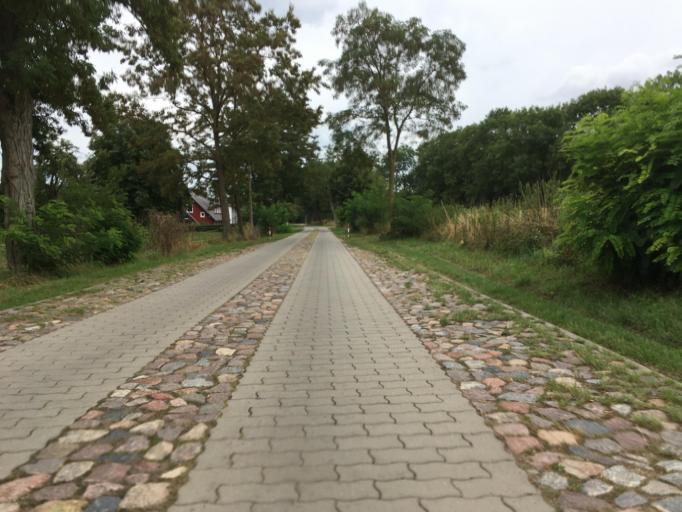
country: DE
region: Brandenburg
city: Passow
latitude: 53.1642
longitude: 14.0971
